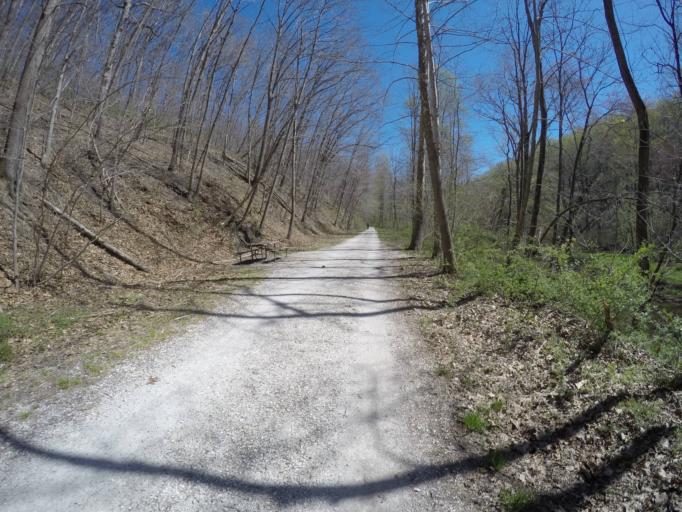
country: US
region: Maryland
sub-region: Baltimore County
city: Hunt Valley
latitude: 39.5965
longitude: -76.6234
